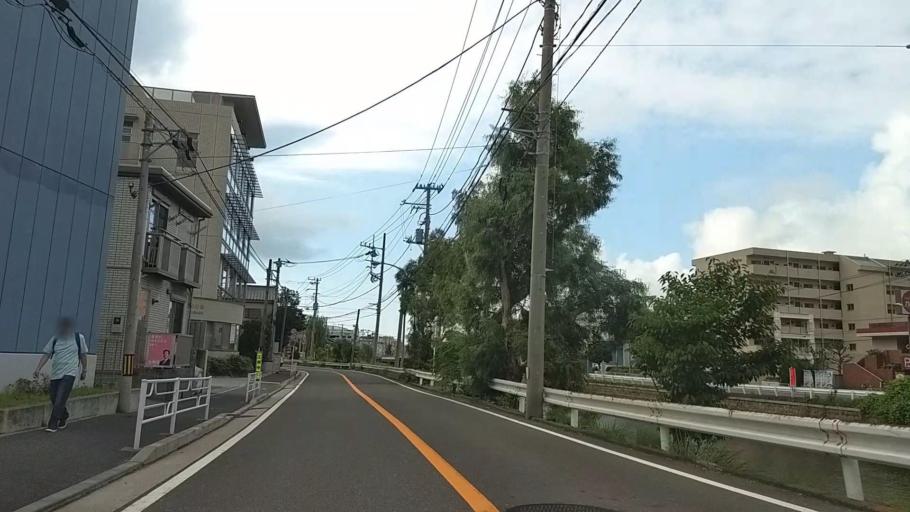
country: JP
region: Kanagawa
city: Yokohama
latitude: 35.4291
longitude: 139.6219
